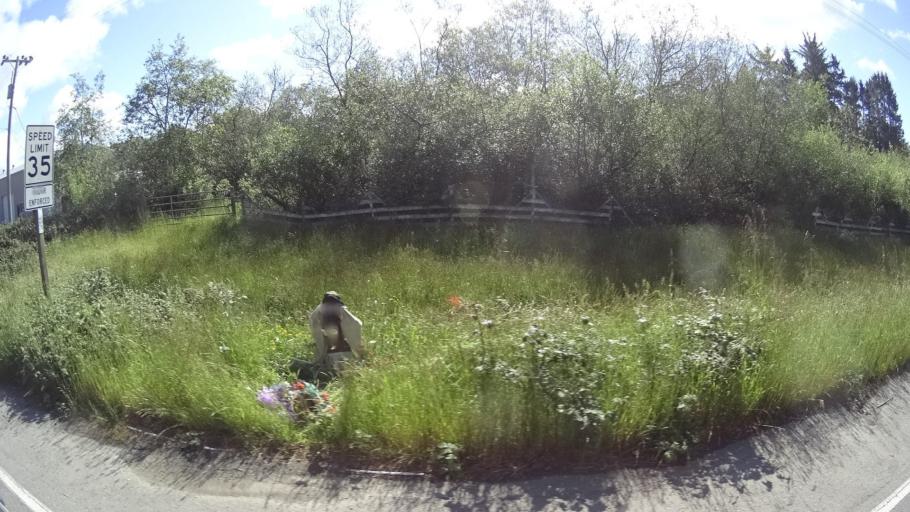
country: US
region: California
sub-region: Humboldt County
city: McKinleyville
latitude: 40.9505
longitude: -124.1009
